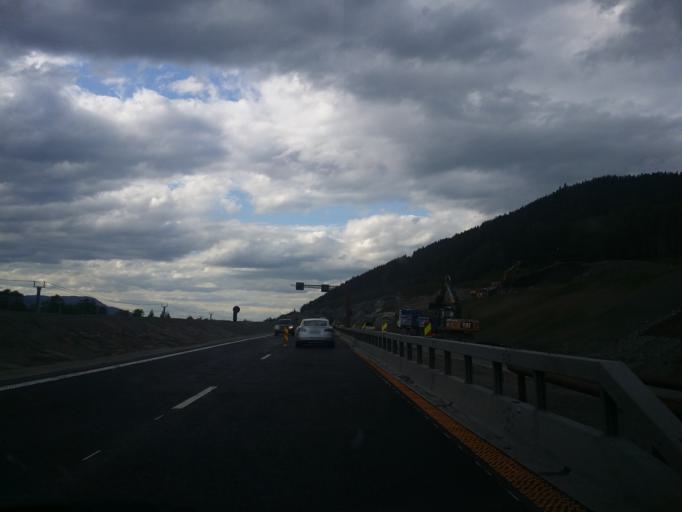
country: NO
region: Akershus
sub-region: Eidsvoll
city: Eidsvoll
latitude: 60.4423
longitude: 11.2420
